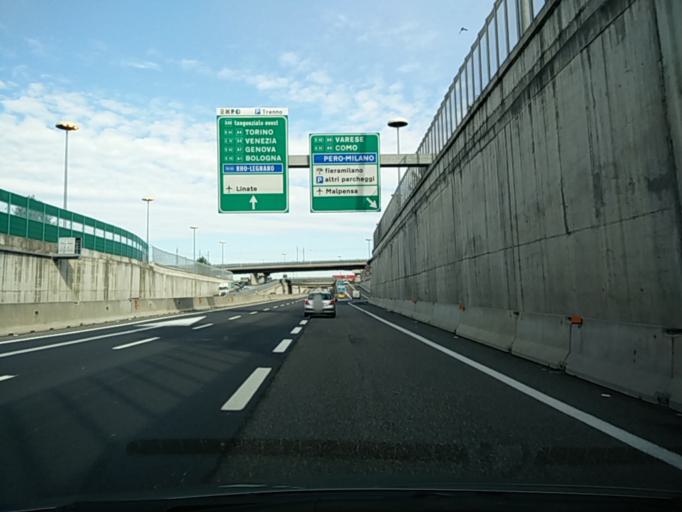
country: IT
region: Lombardy
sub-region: Citta metropolitana di Milano
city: Rho
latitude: 45.5212
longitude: 9.0668
